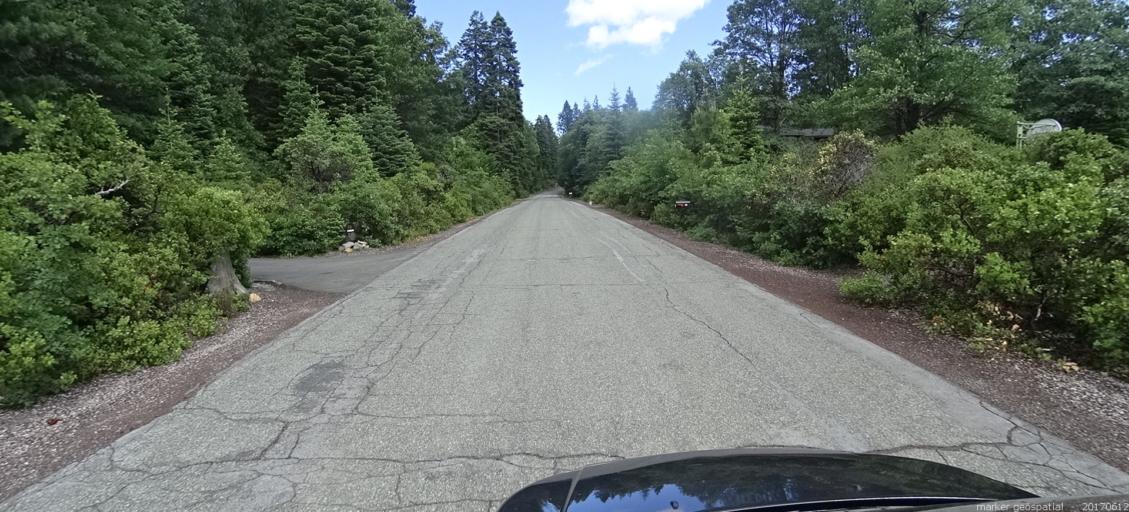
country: US
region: California
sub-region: Siskiyou County
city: Mount Shasta
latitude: 41.3141
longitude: -122.2829
